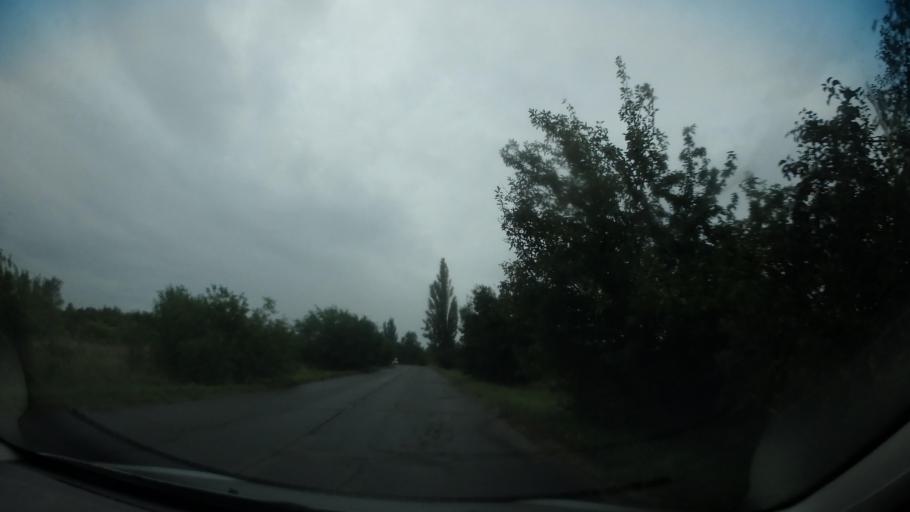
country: CZ
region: Central Bohemia
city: Milovice
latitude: 50.2363
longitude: 14.8972
